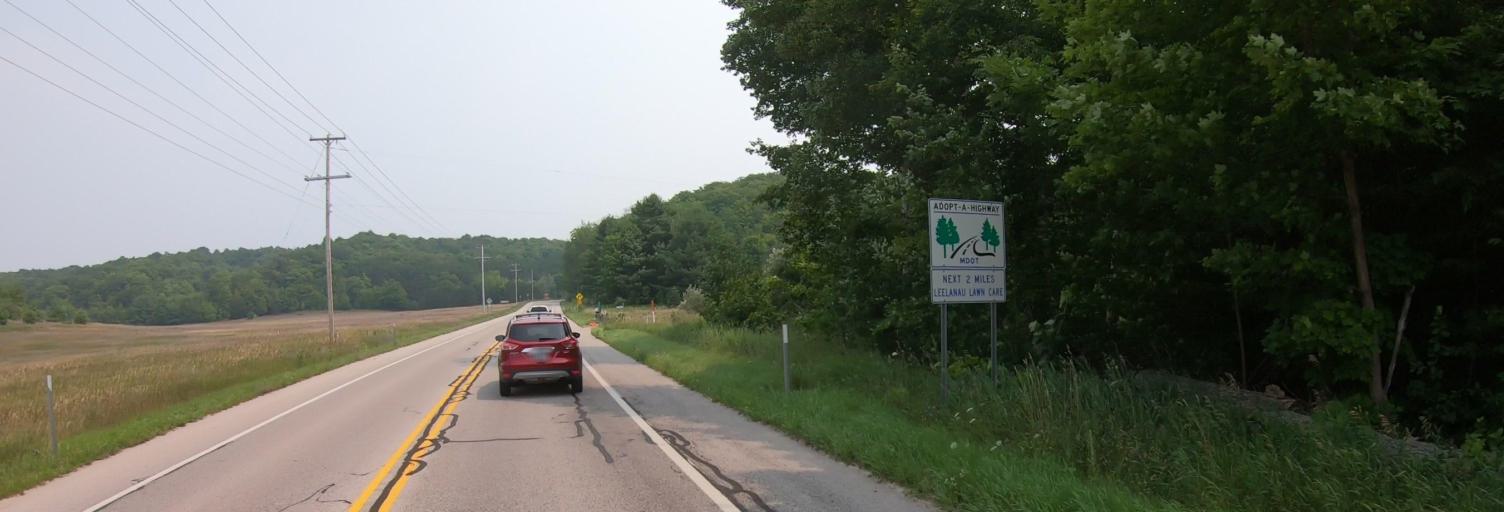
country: US
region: Michigan
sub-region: Leelanau County
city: Leland
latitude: 45.0989
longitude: -85.6582
